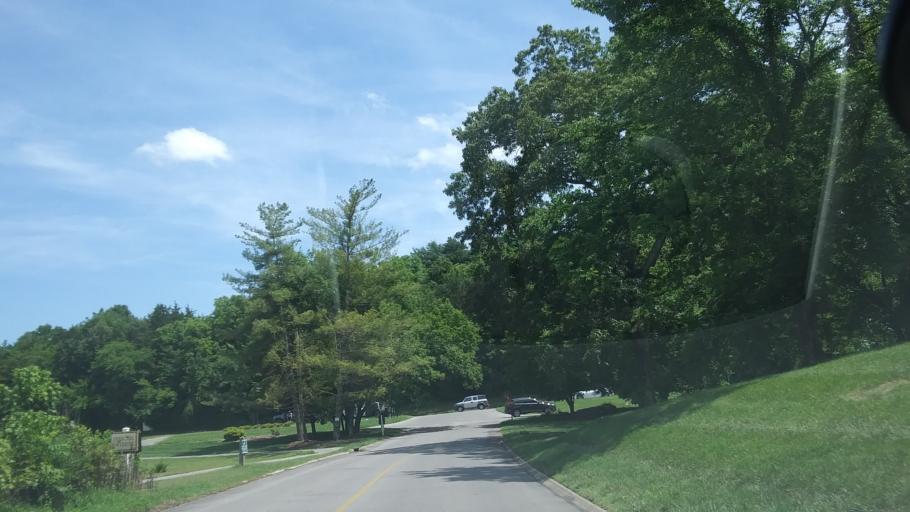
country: US
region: Tennessee
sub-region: Rutherford County
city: La Vergne
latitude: 36.0899
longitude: -86.6438
